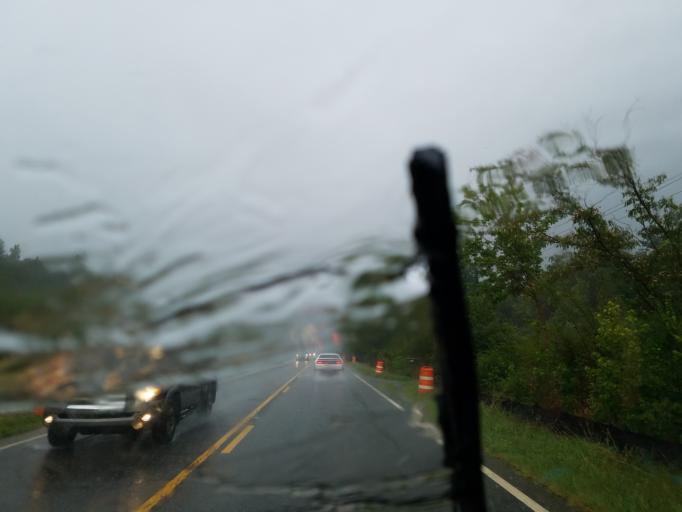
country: US
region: Georgia
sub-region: Floyd County
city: Shannon
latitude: 34.3687
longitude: -85.0131
